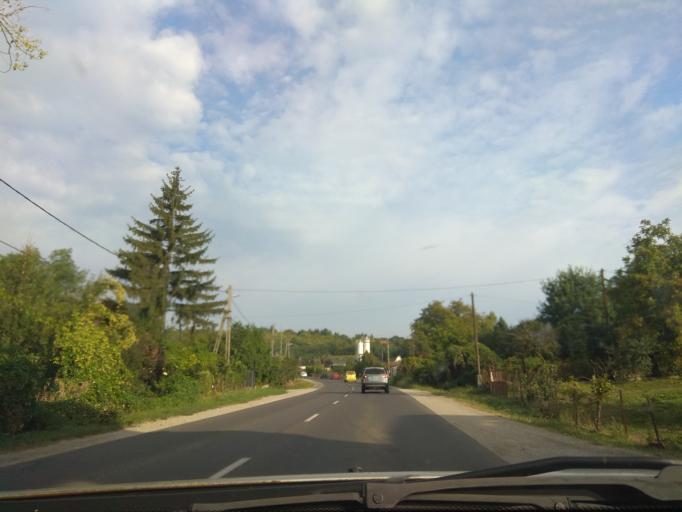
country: HU
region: Borsod-Abauj-Zemplen
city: Miskolc
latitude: 48.0871
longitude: 20.7687
